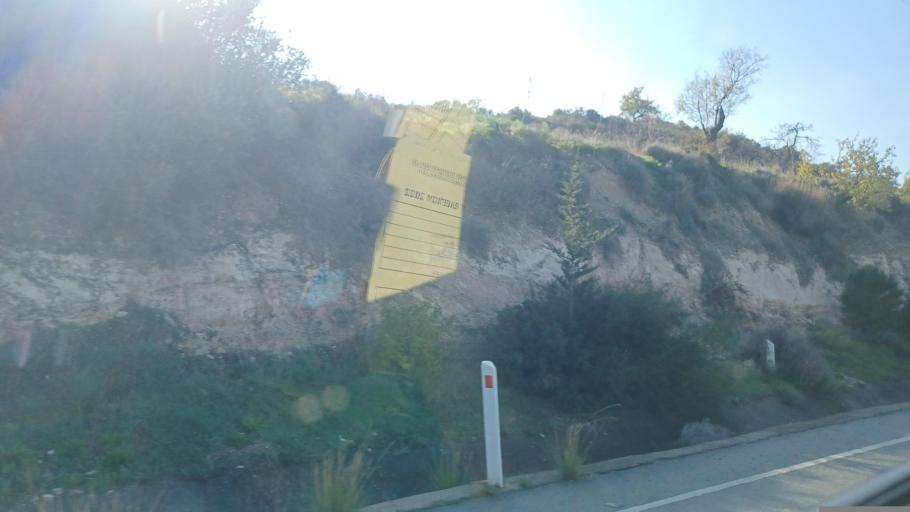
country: CY
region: Larnaka
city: Kofinou
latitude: 34.8484
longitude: 33.3019
